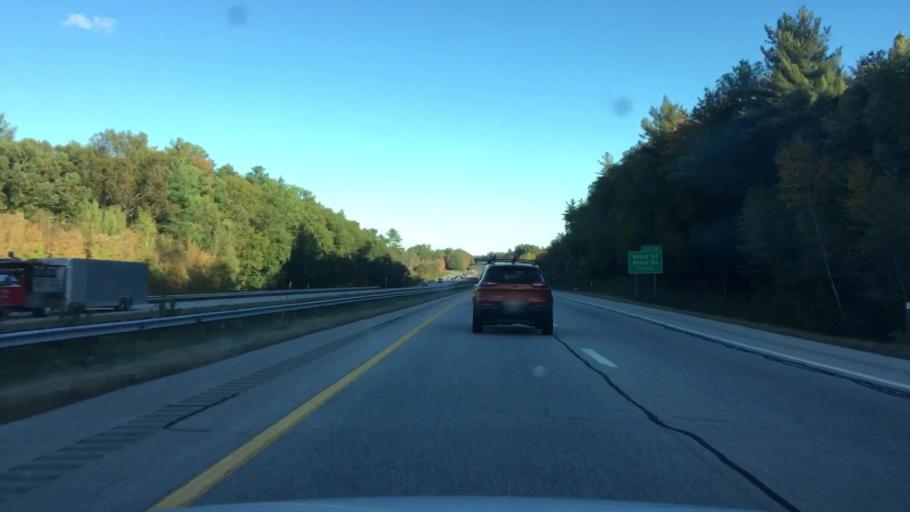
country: US
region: New Hampshire
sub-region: Rockingham County
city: Fremont
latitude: 43.0307
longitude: -71.1304
